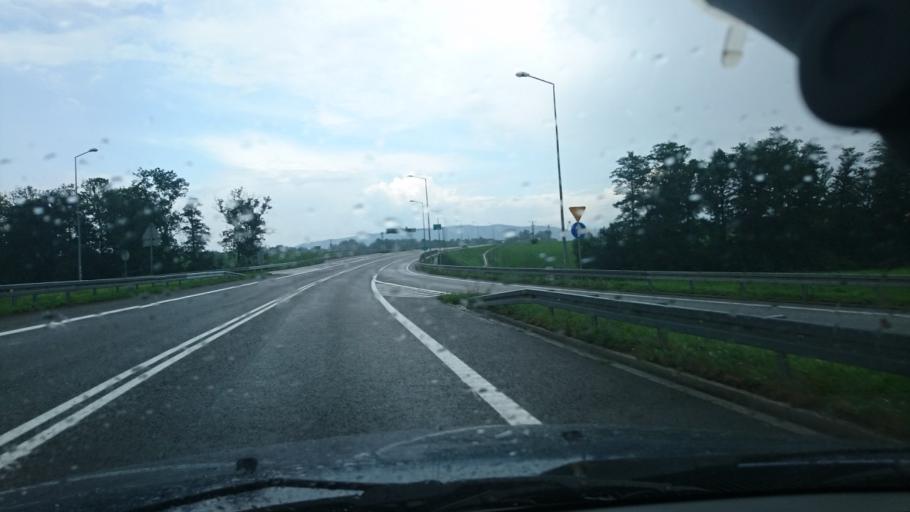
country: PL
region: Silesian Voivodeship
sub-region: Powiat zywiecki
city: Wieprz
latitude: 49.6589
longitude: 19.1667
